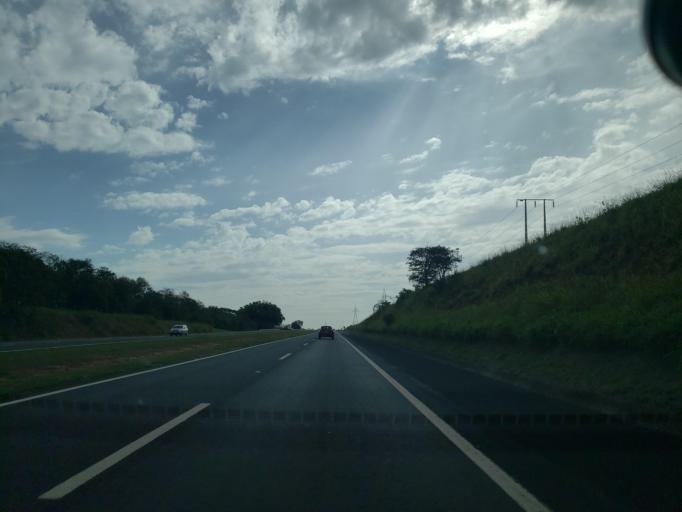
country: BR
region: Sao Paulo
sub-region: Lins
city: Lins
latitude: -21.7393
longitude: -49.7005
